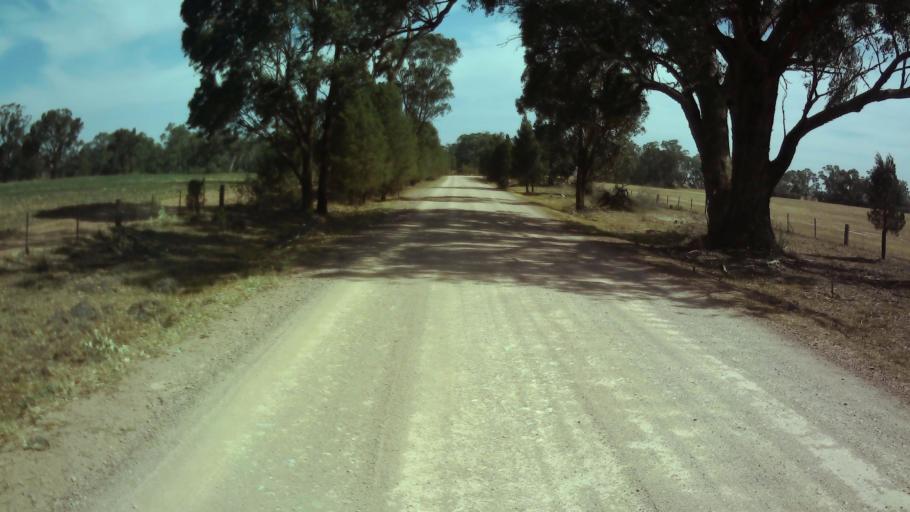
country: AU
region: New South Wales
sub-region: Weddin
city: Grenfell
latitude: -34.0382
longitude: 148.0807
